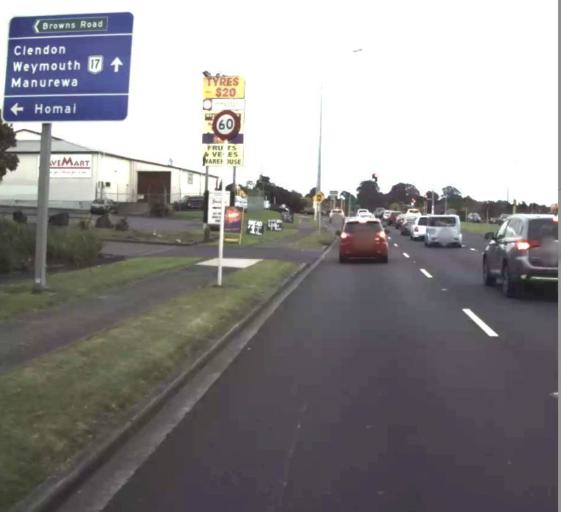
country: NZ
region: Auckland
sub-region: Auckland
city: Wiri
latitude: -37.0177
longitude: 174.8616
